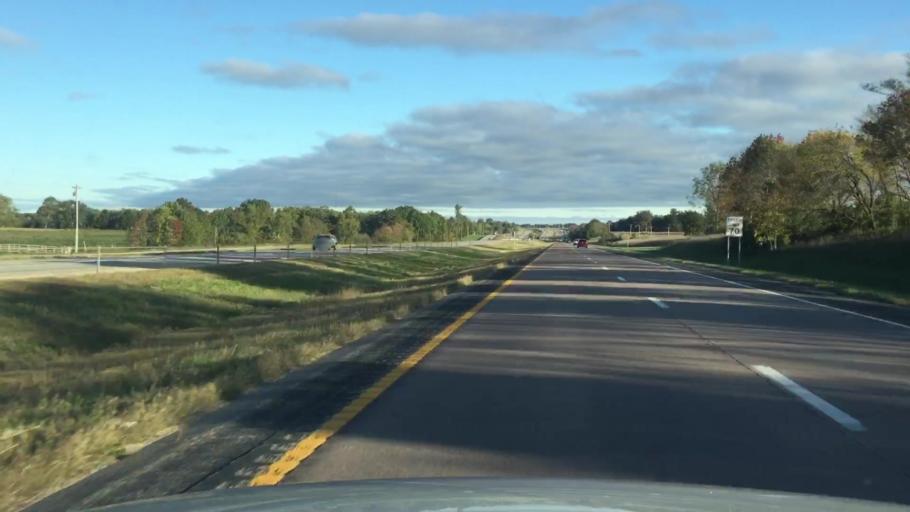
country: US
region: Missouri
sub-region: Boone County
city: Ashland
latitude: 38.8422
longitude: -92.2491
